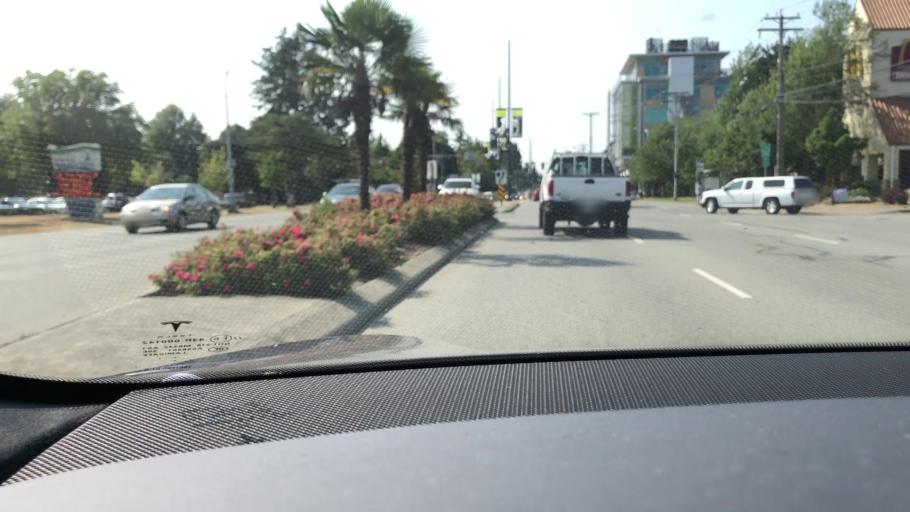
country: US
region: Washington
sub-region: Whatcom County
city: Point Roberts
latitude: 49.0364
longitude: -123.0687
